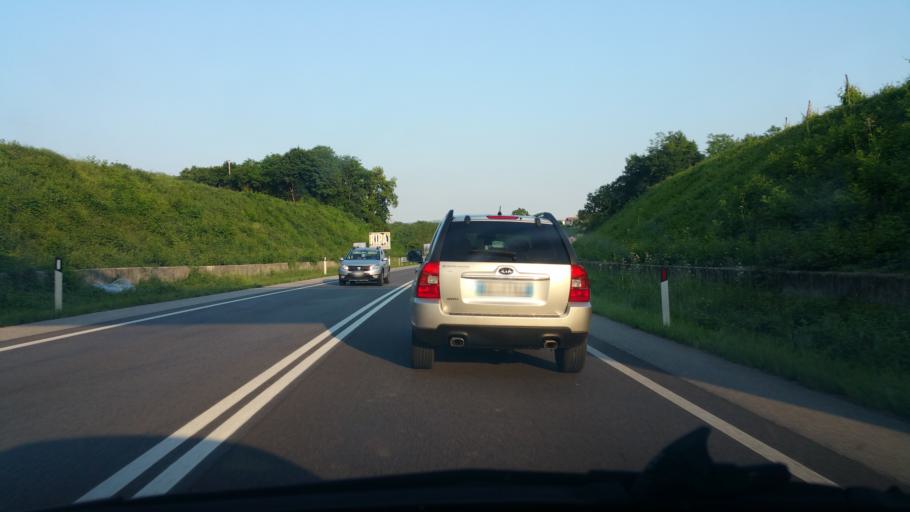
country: IT
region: Veneto
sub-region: Provincia di Treviso
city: Onigo
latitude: 45.8640
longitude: 11.9902
